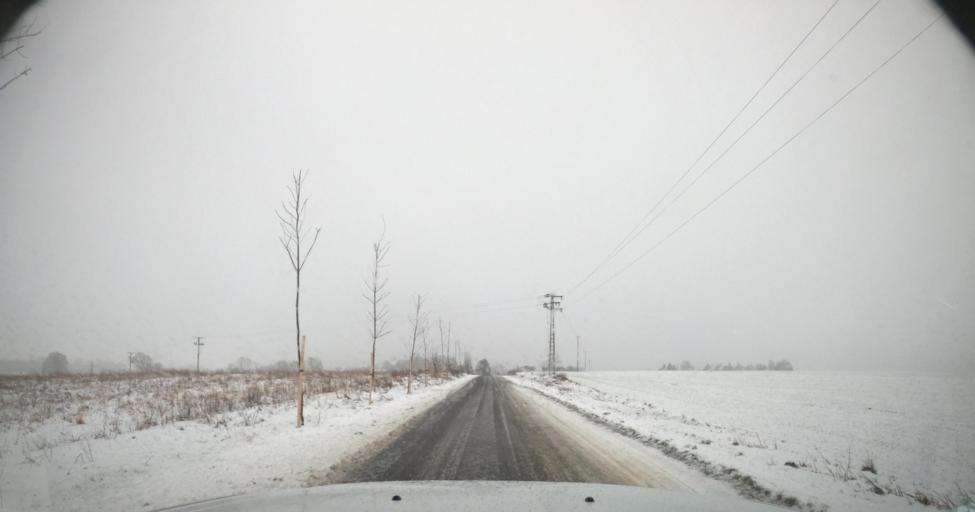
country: PL
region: West Pomeranian Voivodeship
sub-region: Powiat kamienski
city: Golczewo
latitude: 53.7915
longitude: 14.9501
